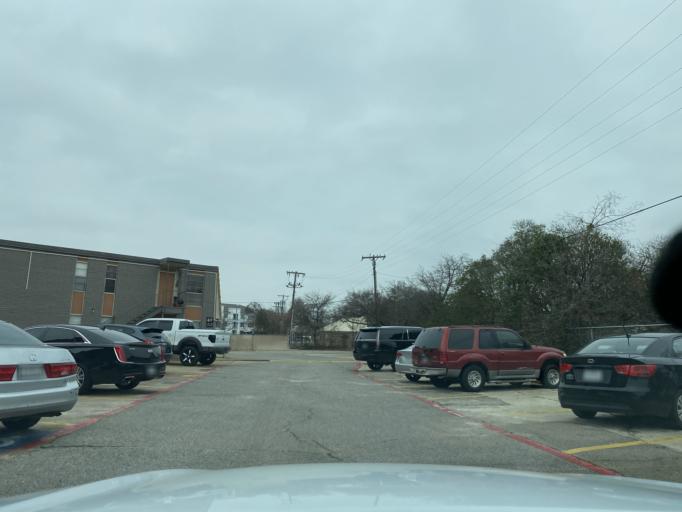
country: US
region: Texas
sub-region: Tarrant County
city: Euless
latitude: 32.8293
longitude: -97.0953
